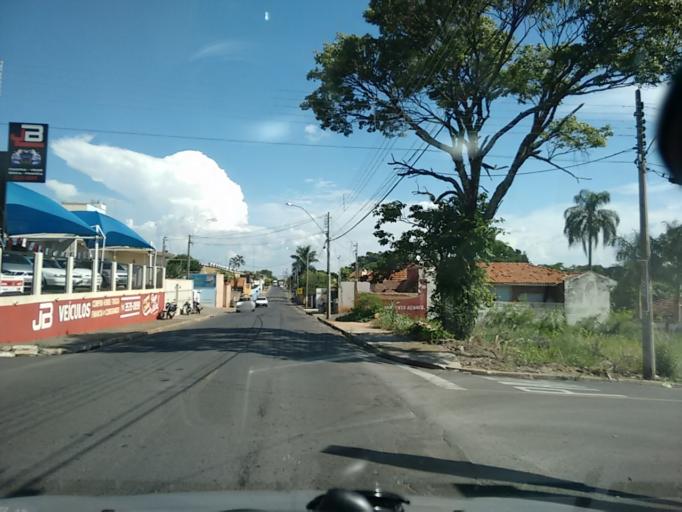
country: BR
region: Sao Paulo
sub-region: Pompeia
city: Pompeia
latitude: -22.1053
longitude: -50.1792
